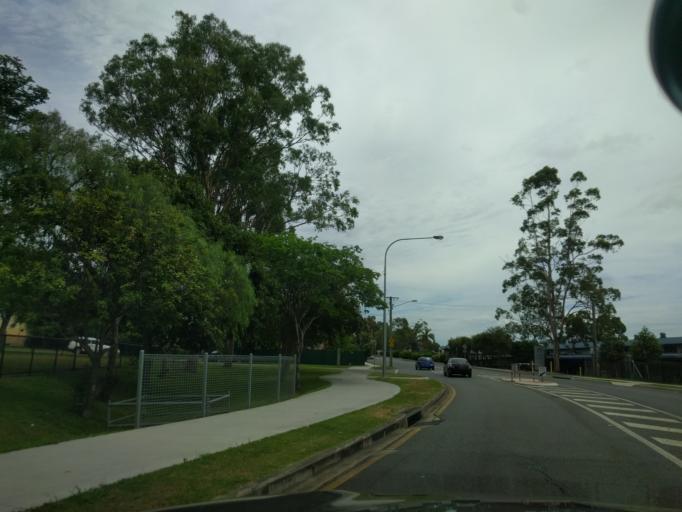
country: AU
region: Queensland
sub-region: Brisbane
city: Stafford
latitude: -27.4127
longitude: 153.0069
